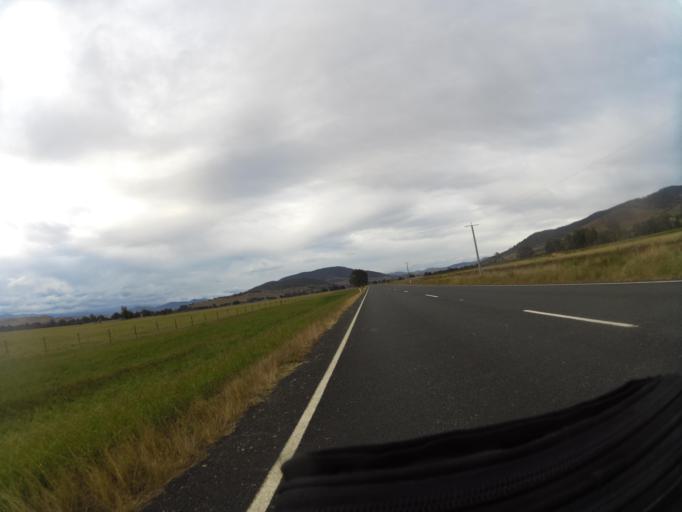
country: AU
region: New South Wales
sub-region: Snowy River
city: Jindabyne
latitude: -36.0995
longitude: 147.9813
